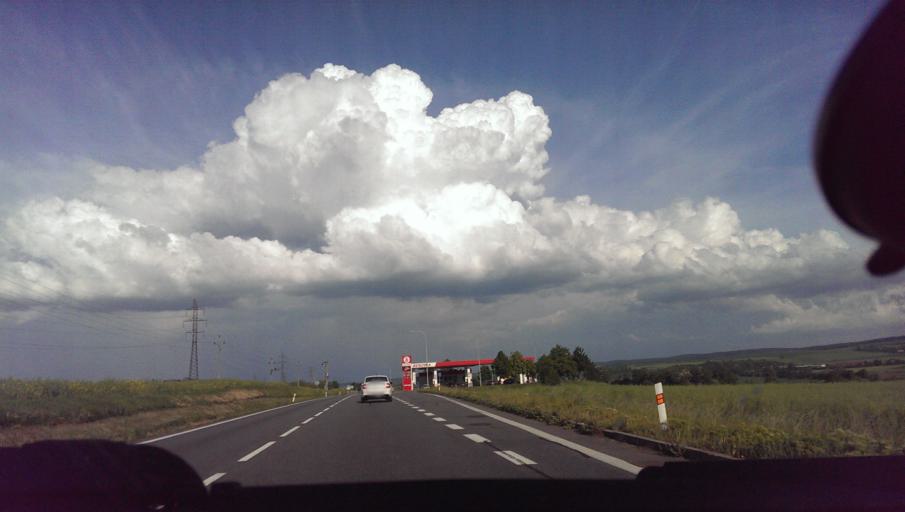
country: CZ
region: South Moravian
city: Slavkov u Brna
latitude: 49.1490
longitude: 16.9199
